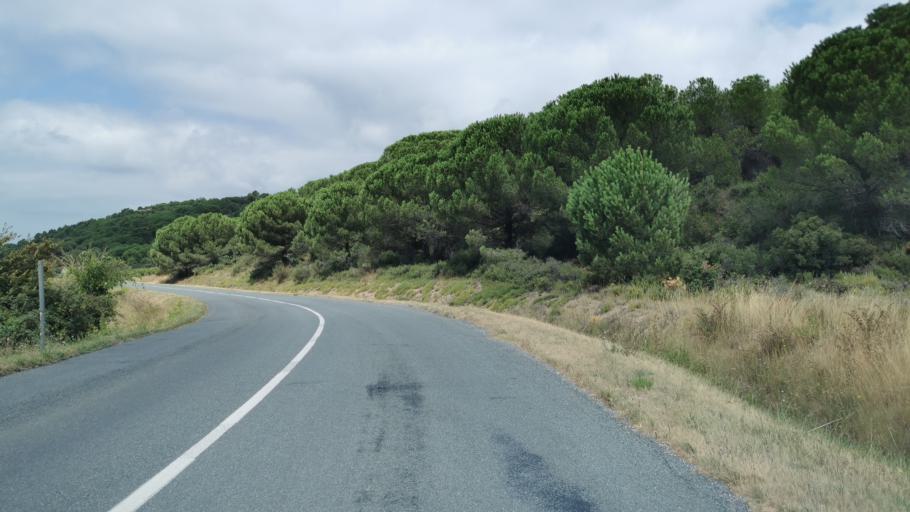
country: FR
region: Languedoc-Roussillon
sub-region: Departement de l'Aude
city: Bizanet
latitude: 43.1623
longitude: 2.8944
